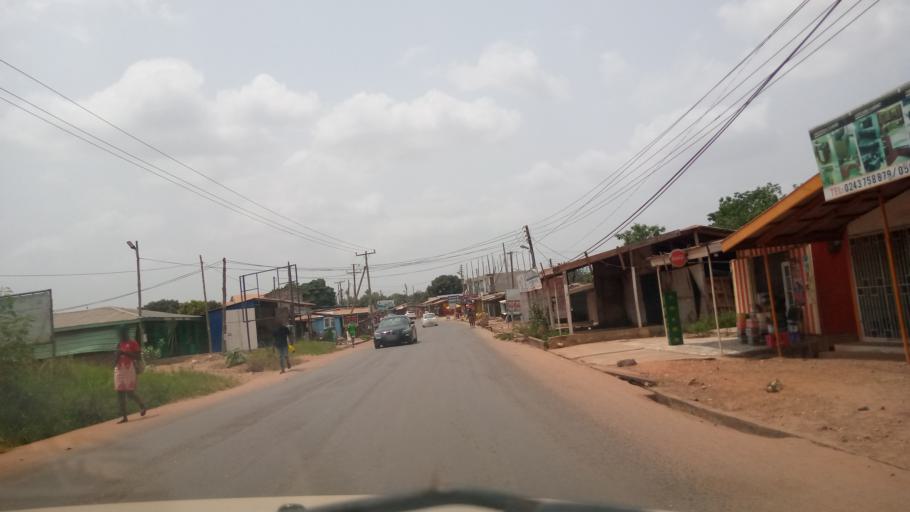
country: GH
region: Greater Accra
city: Dome
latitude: 5.6713
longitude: -0.2048
